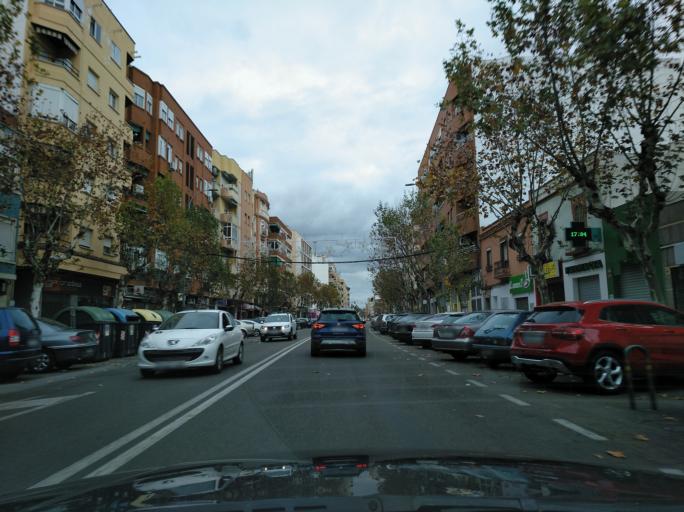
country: ES
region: Extremadura
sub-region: Provincia de Badajoz
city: Badajoz
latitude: 38.8791
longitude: -6.9574
